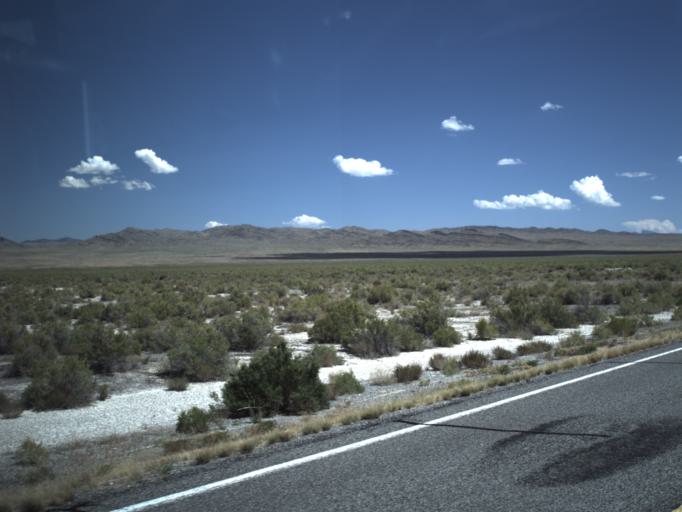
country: US
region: Nevada
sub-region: White Pine County
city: McGill
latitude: 39.0480
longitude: -113.9301
